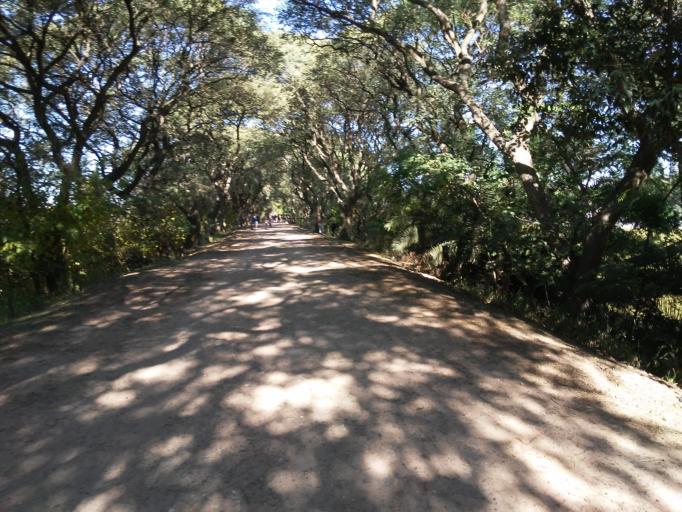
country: AR
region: Buenos Aires F.D.
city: Buenos Aires
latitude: -34.6113
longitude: -58.3568
